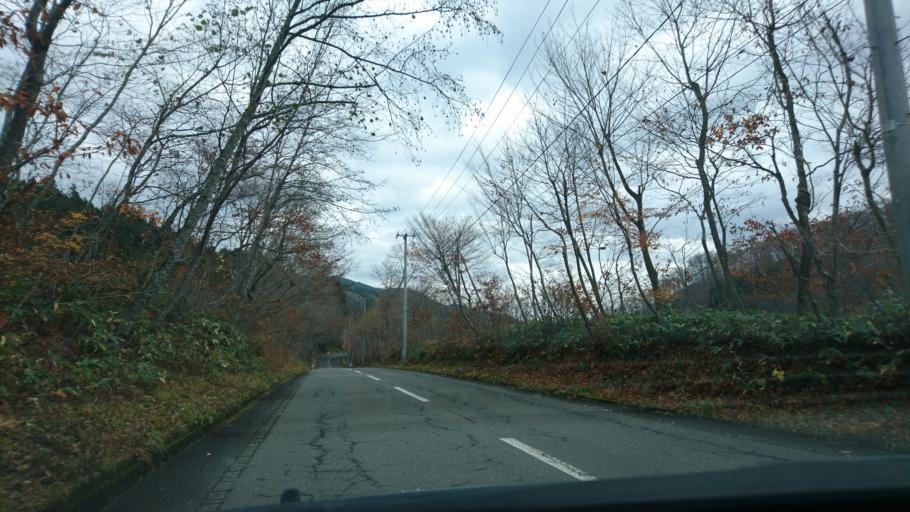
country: JP
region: Iwate
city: Ichinoseki
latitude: 38.9132
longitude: 140.8705
